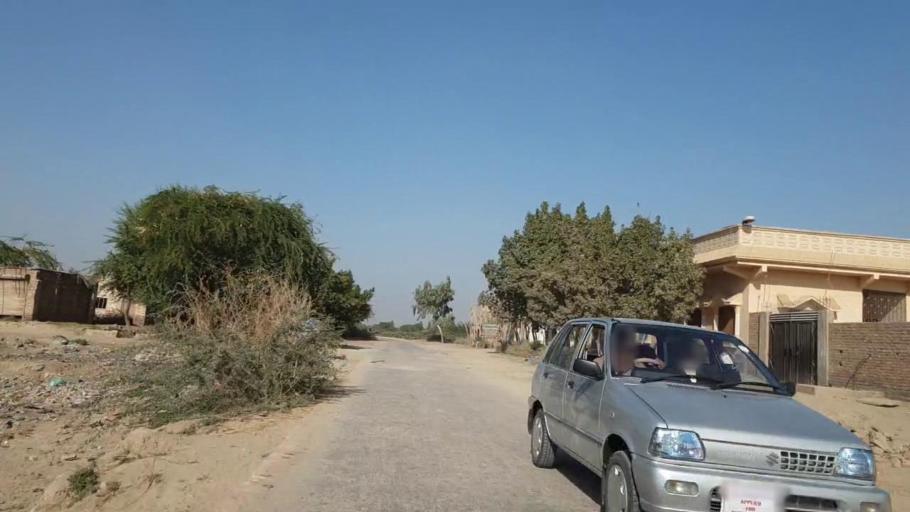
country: PK
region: Sindh
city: Digri
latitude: 25.1295
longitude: 69.1112
